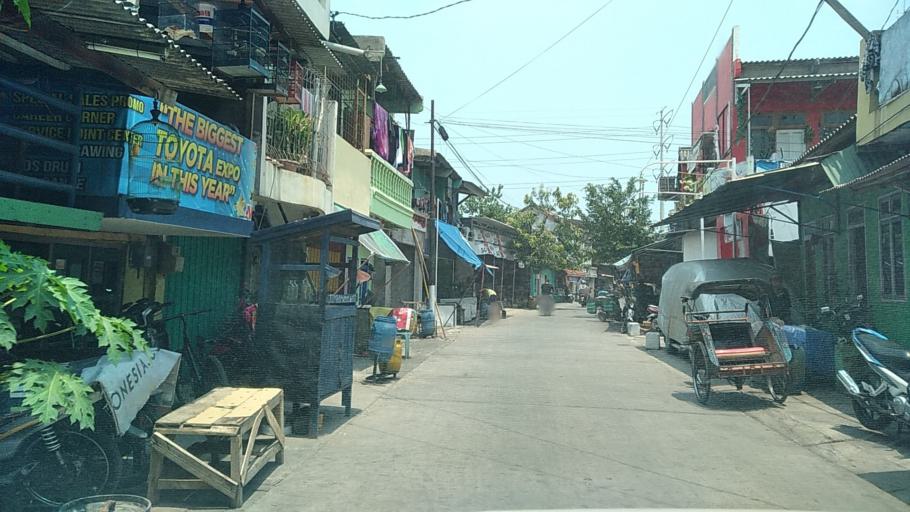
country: ID
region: Central Java
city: Semarang
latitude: -6.9584
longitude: 110.4266
